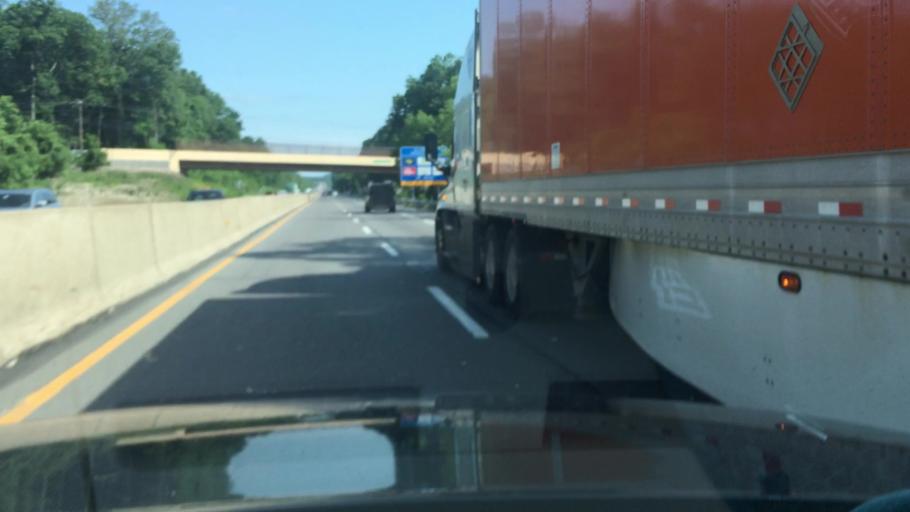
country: US
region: Pennsylvania
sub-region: Bucks County
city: Spinnerstown
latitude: 40.3948
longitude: -75.4110
